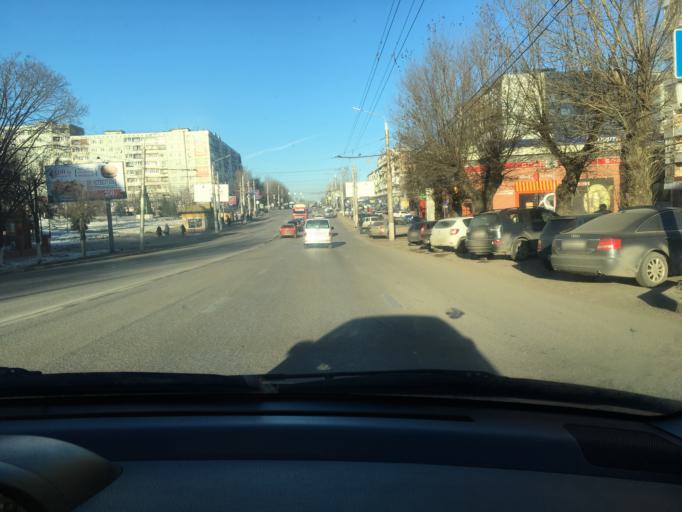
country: RU
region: Tula
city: Tula
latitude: 54.2163
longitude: 37.6241
